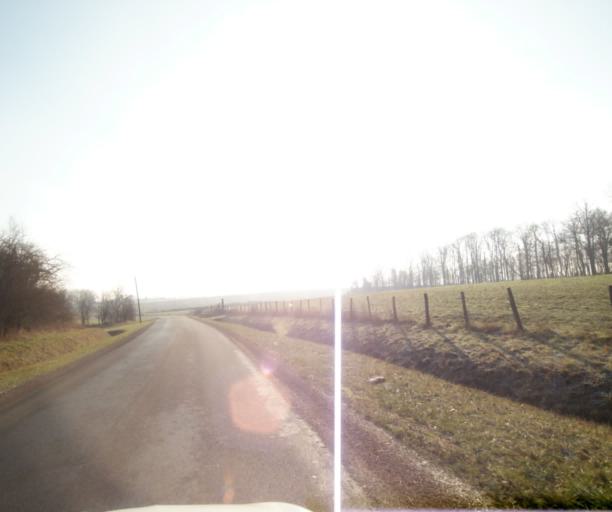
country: FR
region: Champagne-Ardenne
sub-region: Departement de la Haute-Marne
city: Montier-en-Der
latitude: 48.4876
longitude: 4.7384
